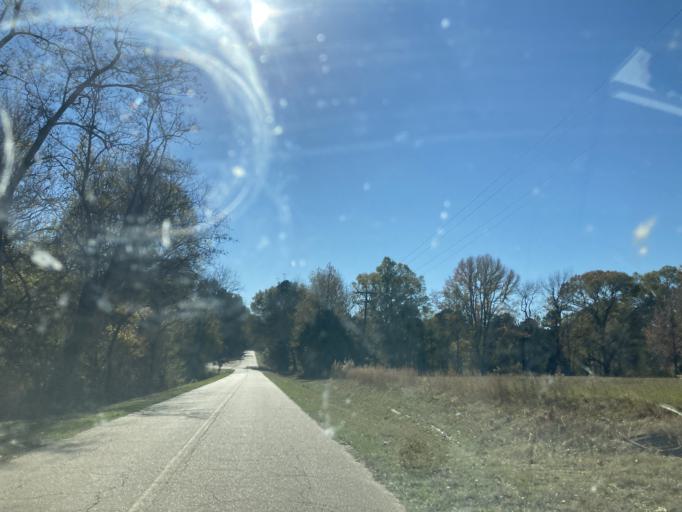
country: US
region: Mississippi
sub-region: Hinds County
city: Lynchburg
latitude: 32.5835
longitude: -90.5697
